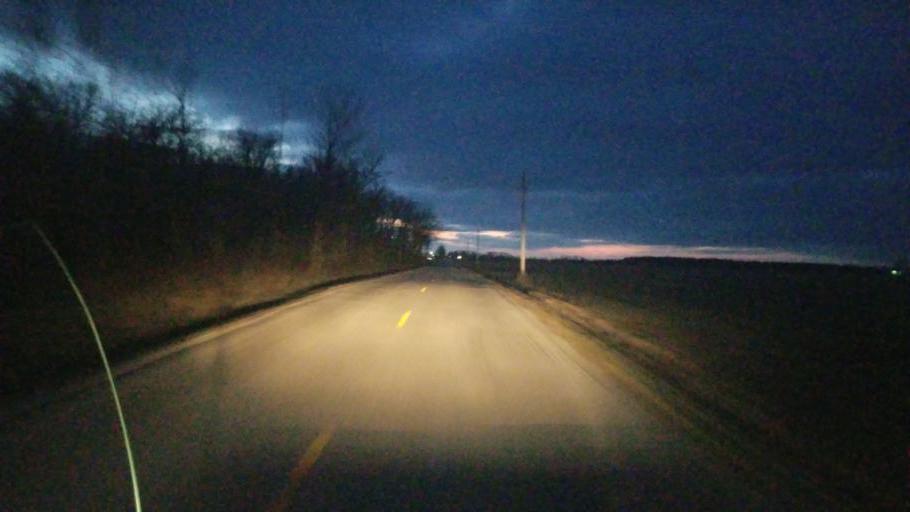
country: US
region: Ohio
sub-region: Marion County
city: Prospect
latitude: 40.4635
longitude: -83.2445
